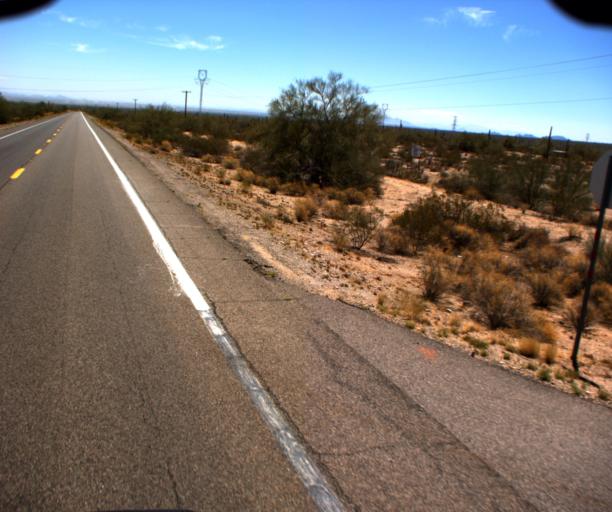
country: US
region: Arizona
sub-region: Pinal County
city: Maricopa
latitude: 32.8405
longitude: -112.1131
